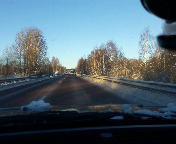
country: SE
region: Gaevleborg
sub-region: Ljusdals Kommun
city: Jaervsoe
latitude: 61.7576
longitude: 16.1608
